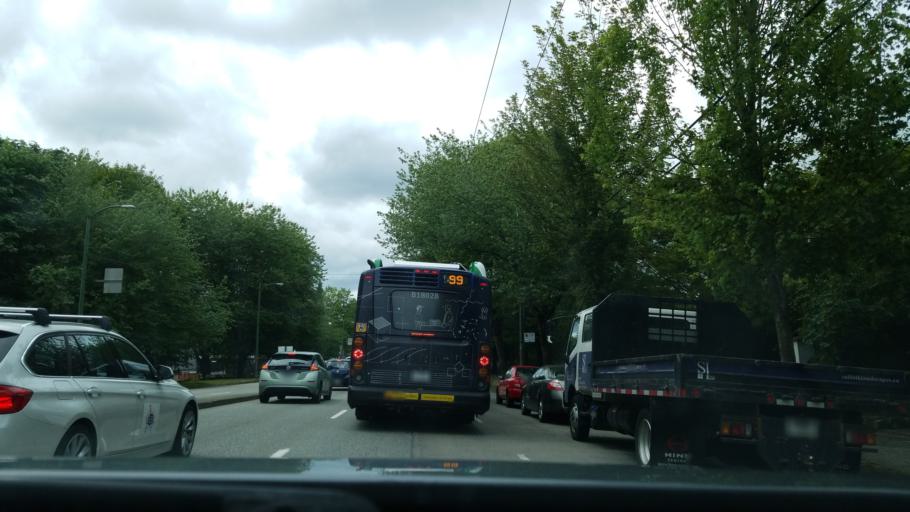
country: CA
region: British Columbia
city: Vancouver
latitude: 49.2624
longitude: -123.0790
